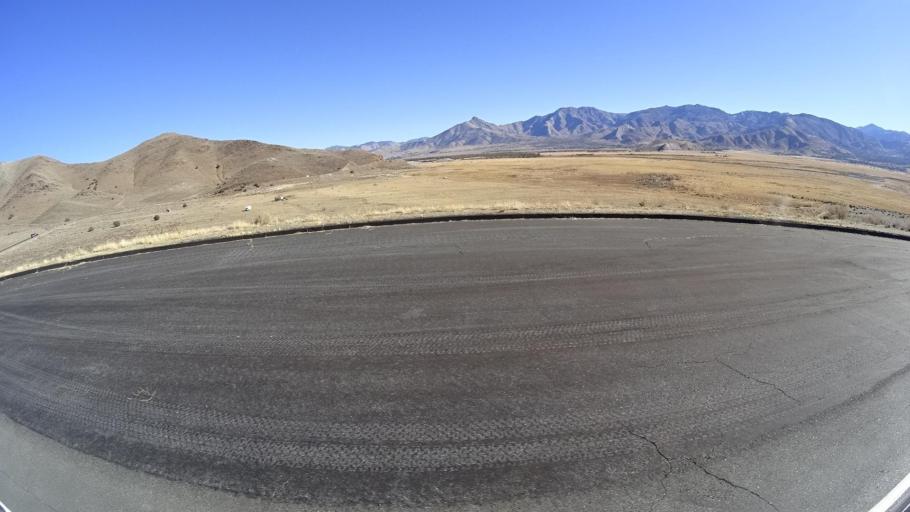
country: US
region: California
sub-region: Kern County
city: Wofford Heights
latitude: 35.6789
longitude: -118.4141
